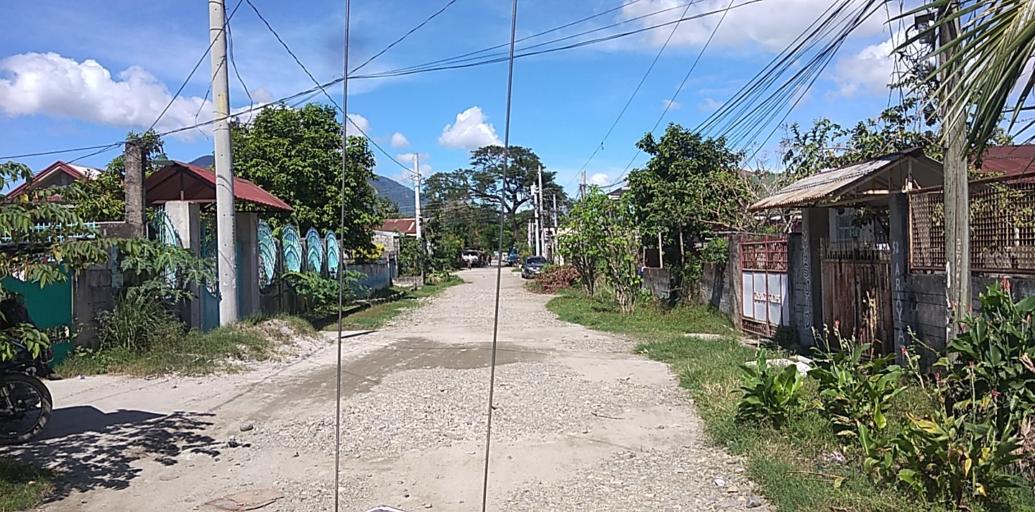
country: PH
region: Central Luzon
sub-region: Province of Pampanga
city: Arayat
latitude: 15.1373
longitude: 120.7747
